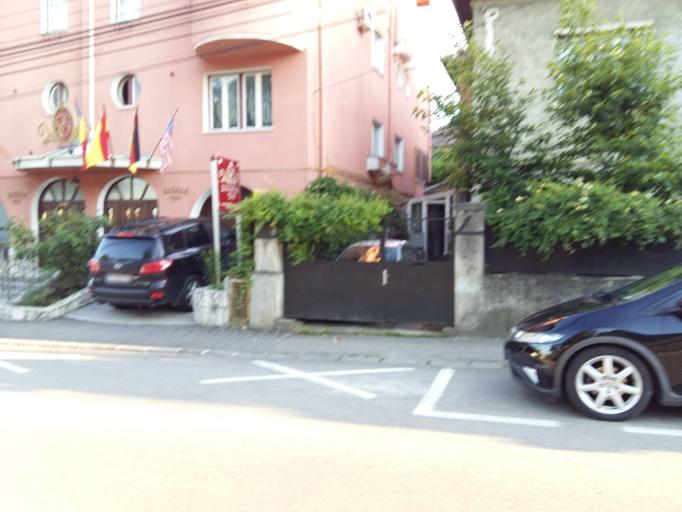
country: RO
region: Cluj
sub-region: Municipiul Cluj-Napoca
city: Cluj-Napoca
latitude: 46.7795
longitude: 23.5835
